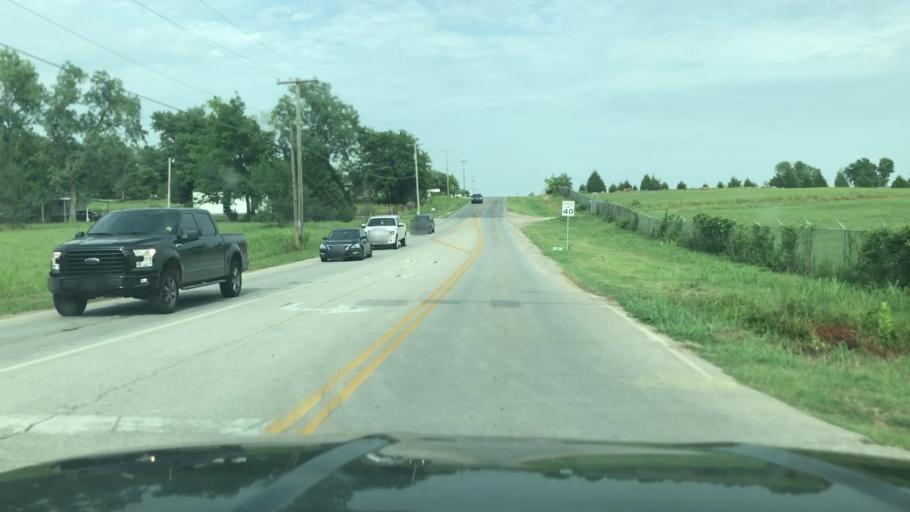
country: US
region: Oklahoma
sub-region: Tulsa County
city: Oakhurst
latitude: 36.0900
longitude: -96.0653
